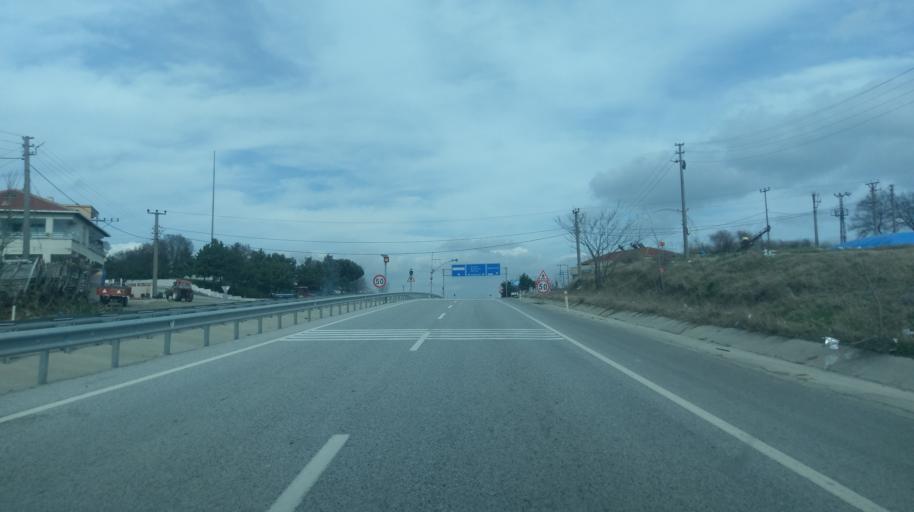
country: TR
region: Edirne
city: Kircasalih
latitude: 41.3896
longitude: 26.7993
